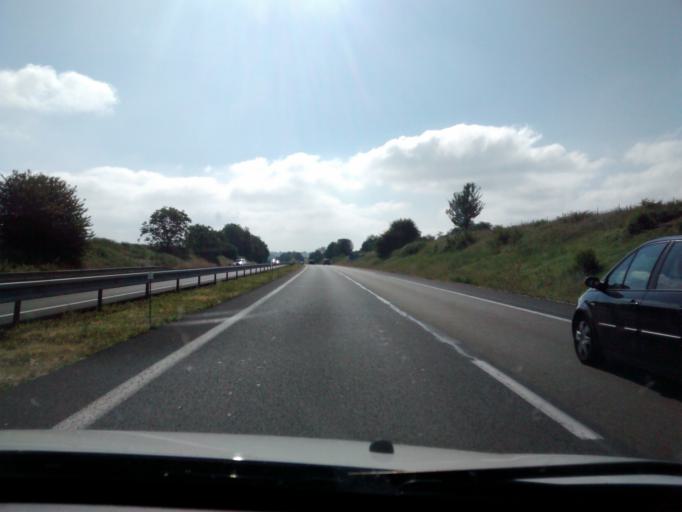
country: FR
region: Pays de la Loire
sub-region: Departement de la Sarthe
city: Brulon
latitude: 48.0034
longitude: -0.2026
